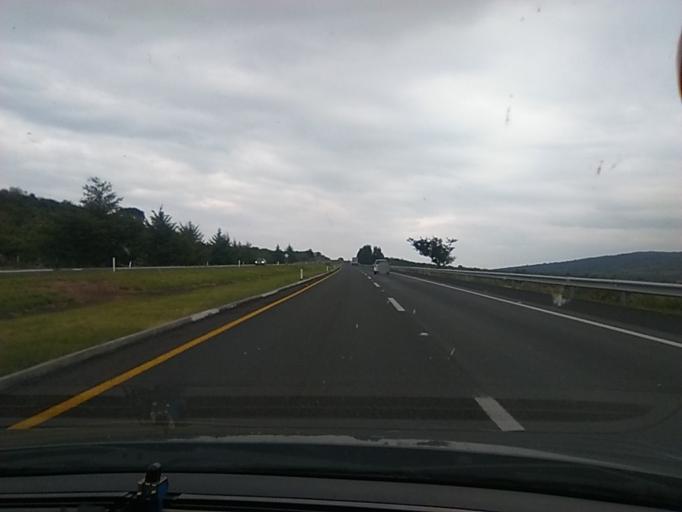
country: MX
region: Michoacan
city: Penjamillo de Degollado
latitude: 20.0150
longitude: -101.9068
